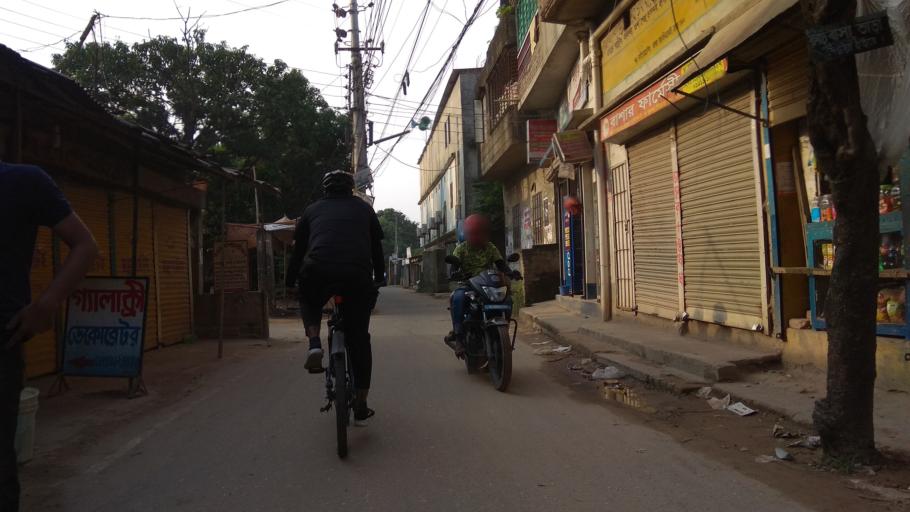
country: BD
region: Dhaka
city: Tungi
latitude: 23.8346
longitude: 90.3880
